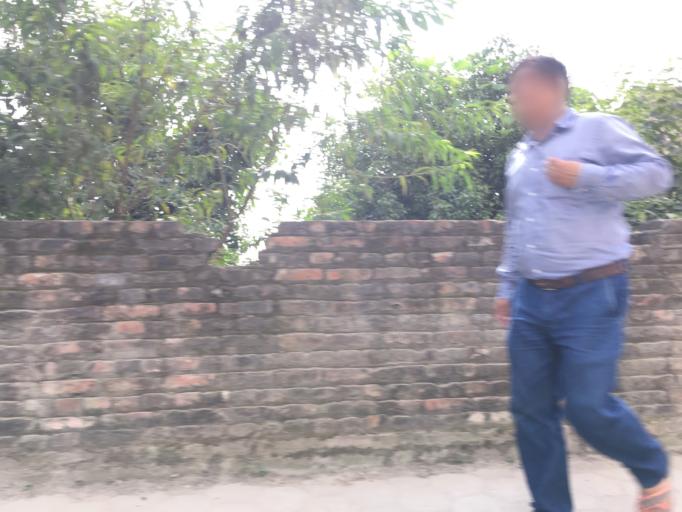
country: NP
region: Central Region
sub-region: Bagmati Zone
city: Kathmandu
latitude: 27.7377
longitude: 85.3487
